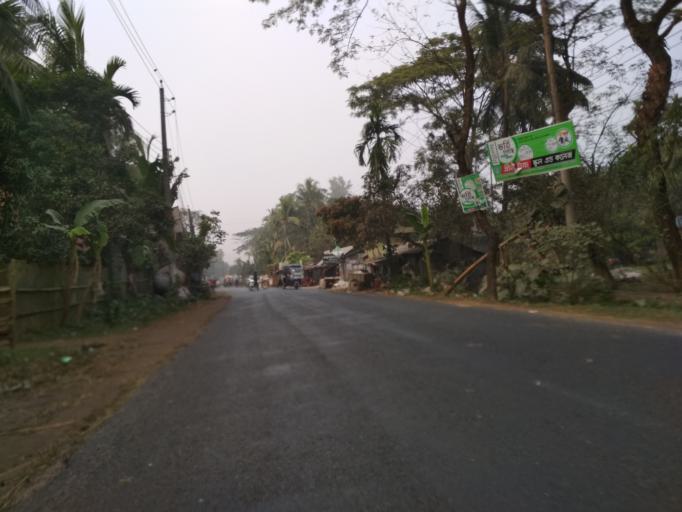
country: BD
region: Chittagong
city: Lakshmipur
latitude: 22.9280
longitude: 90.8338
